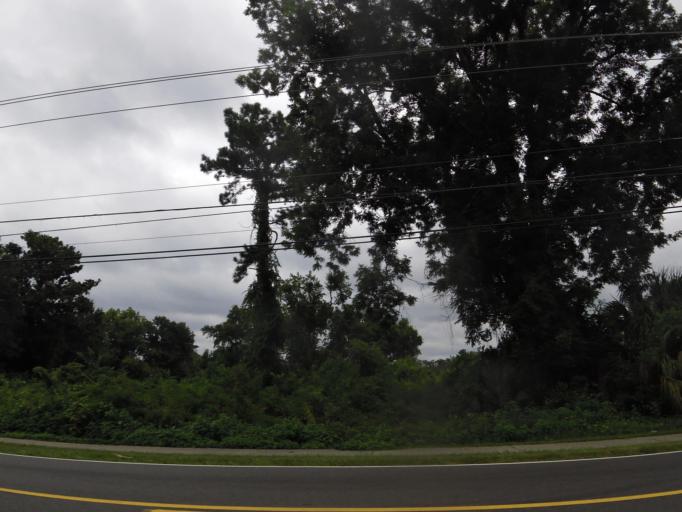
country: US
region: Georgia
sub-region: Glynn County
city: Saint Simon Mills
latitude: 31.1605
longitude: -81.3917
